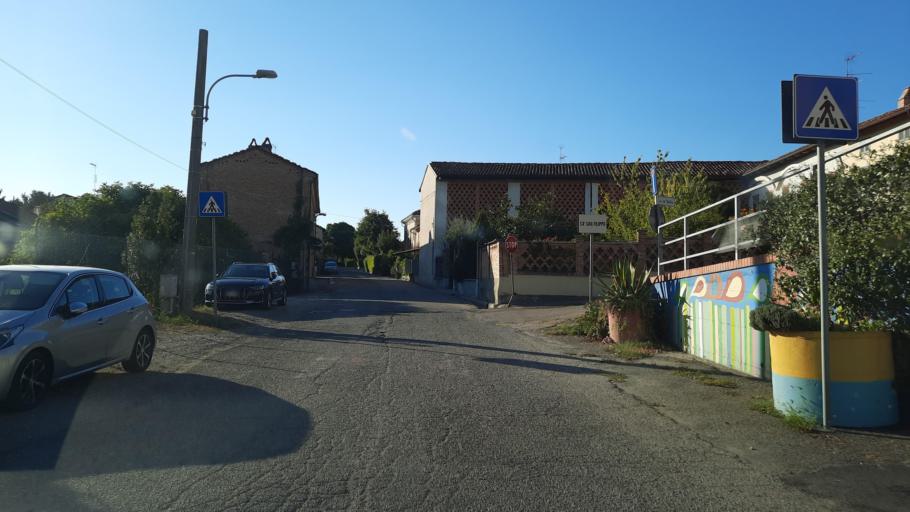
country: IT
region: Piedmont
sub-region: Provincia di Alessandria
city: Camagna Monferrato
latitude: 45.0029
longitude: 8.4165
